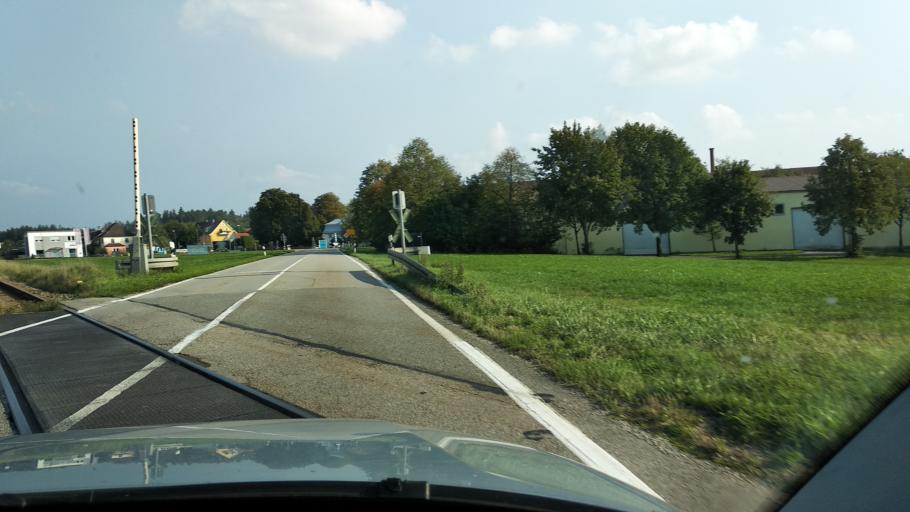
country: DE
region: Bavaria
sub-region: Upper Bavaria
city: Pfaffing
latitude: 48.0830
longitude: 12.0887
